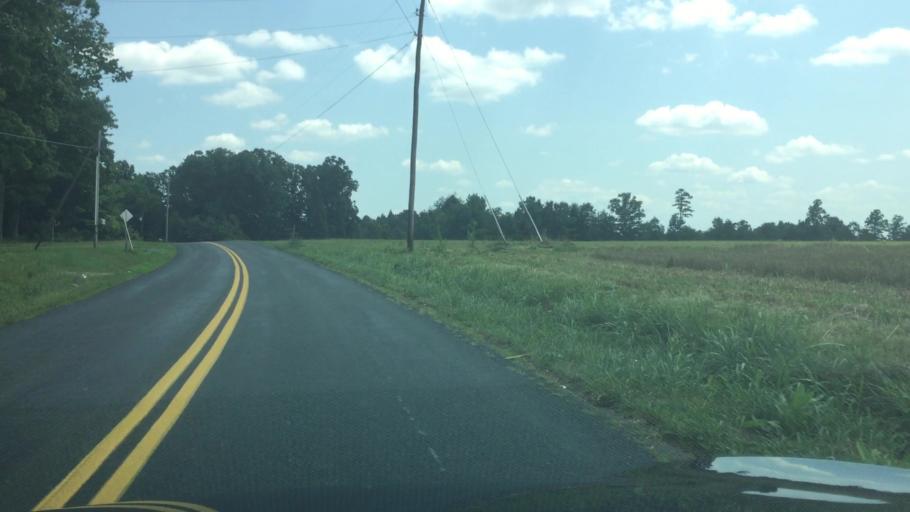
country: US
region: Virginia
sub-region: Appomattox County
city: Appomattox
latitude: 37.2851
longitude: -78.8517
